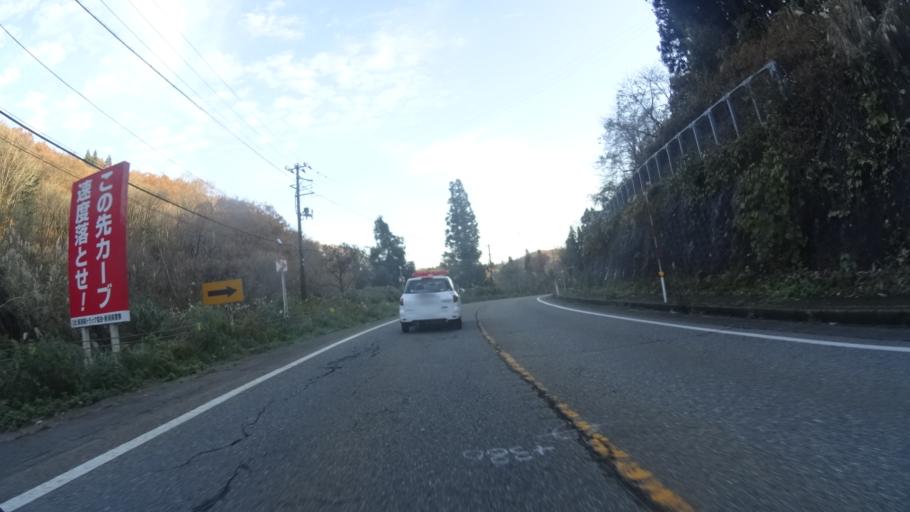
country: JP
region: Niigata
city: Kashiwazaki
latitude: 37.4119
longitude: 138.6846
